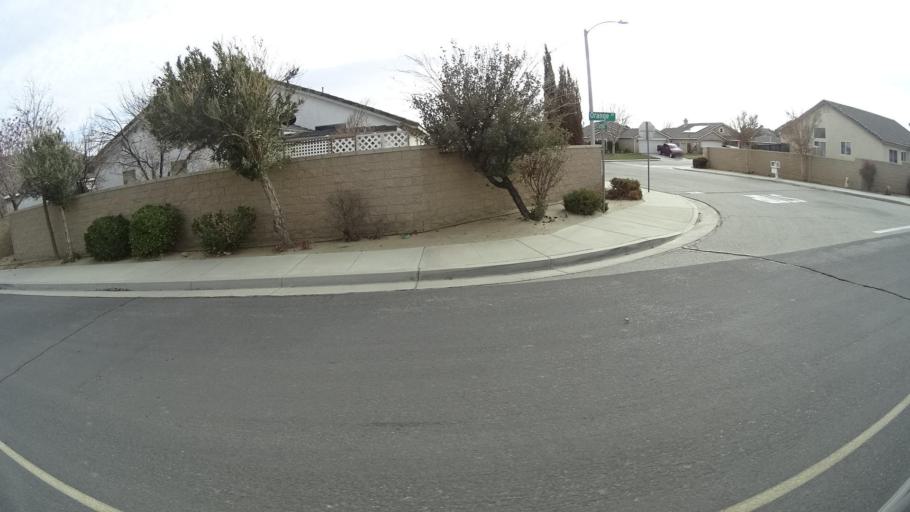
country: US
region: California
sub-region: Kern County
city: Rosamond
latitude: 34.8565
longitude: -118.2007
